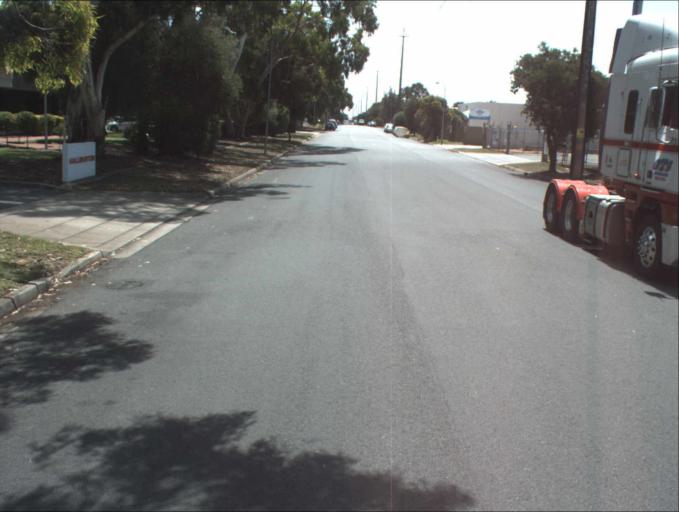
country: AU
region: South Australia
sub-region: Port Adelaide Enfield
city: Blair Athol
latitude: -34.8590
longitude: 138.5702
